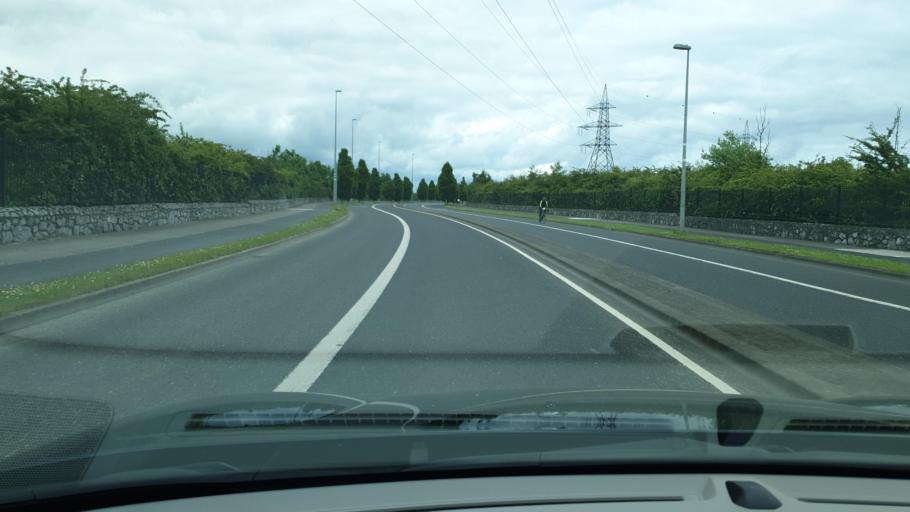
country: IE
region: Leinster
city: Lucan
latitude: 53.3360
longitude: -6.4335
